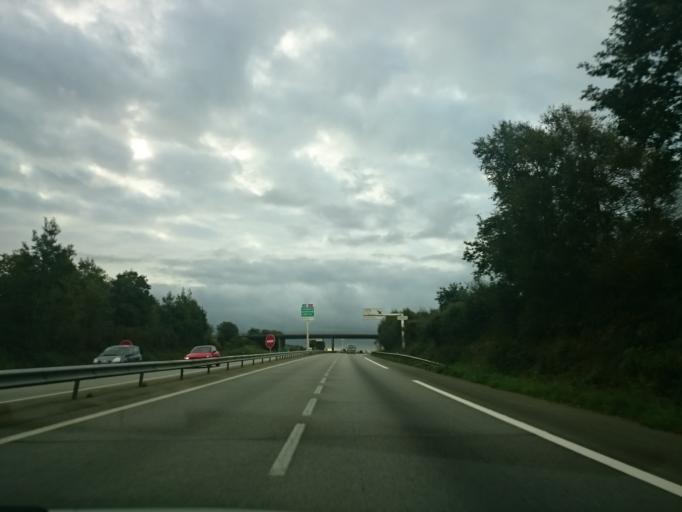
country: FR
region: Brittany
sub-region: Departement du Finistere
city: Chateaulin
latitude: 48.1617
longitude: -4.0436
